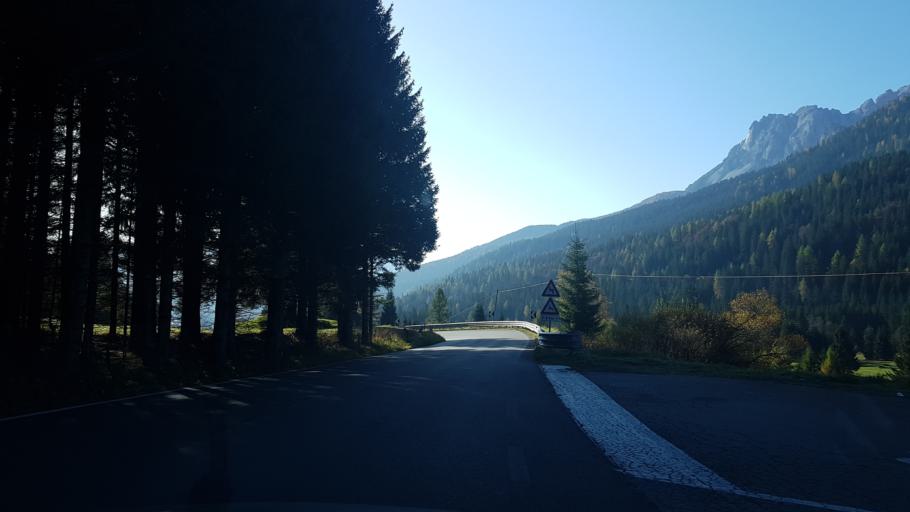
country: IT
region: Veneto
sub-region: Provincia di Belluno
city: Candide
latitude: 46.6233
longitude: 12.4707
